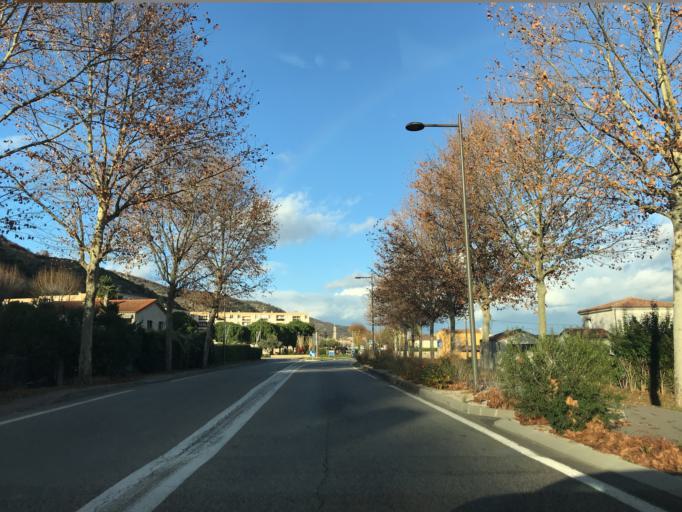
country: FR
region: Rhone-Alpes
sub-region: Departement de l'Ardeche
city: Le Pouzin
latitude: 44.7462
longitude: 4.7452
